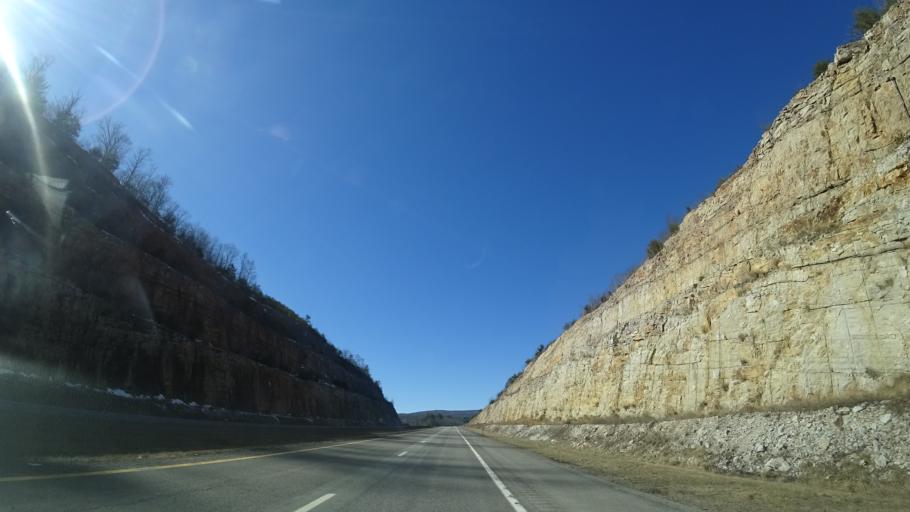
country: US
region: Virginia
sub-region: Shenandoah County
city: Basye
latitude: 39.0428
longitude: -78.7156
